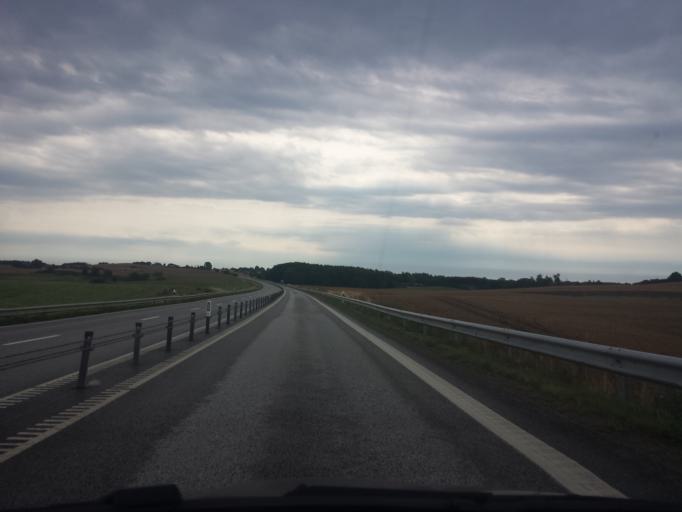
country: SE
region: Skane
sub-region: Ystads Kommun
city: Ystad
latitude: 55.4624
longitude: 13.7225
